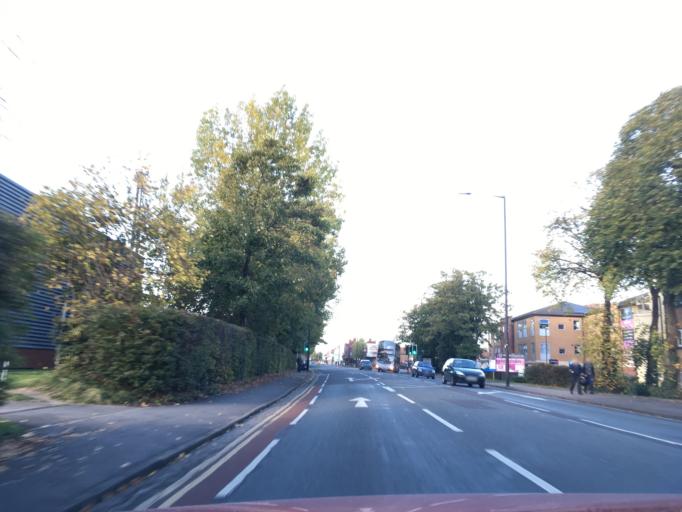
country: GB
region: England
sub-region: Bristol
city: Bristol
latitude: 51.4930
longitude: -2.5831
